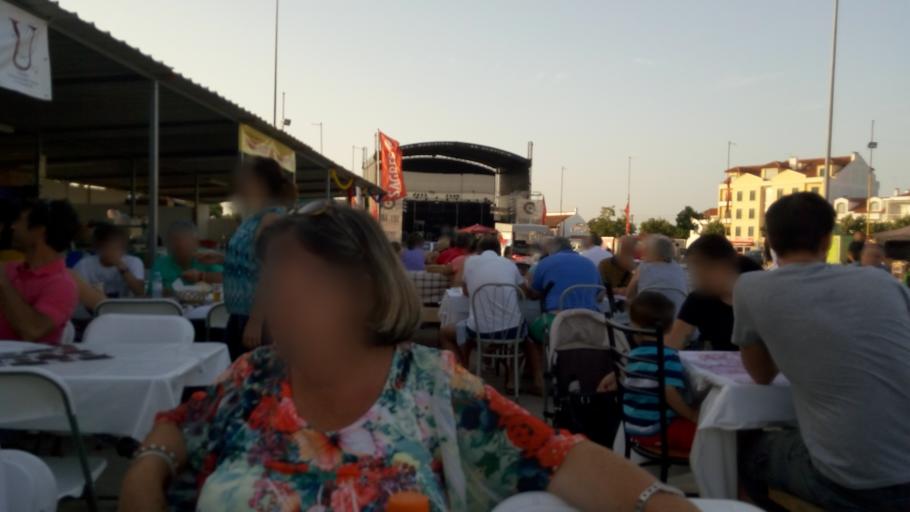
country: PT
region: Santarem
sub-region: Almeirim
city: Almeirim
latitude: 39.1997
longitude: -8.6265
